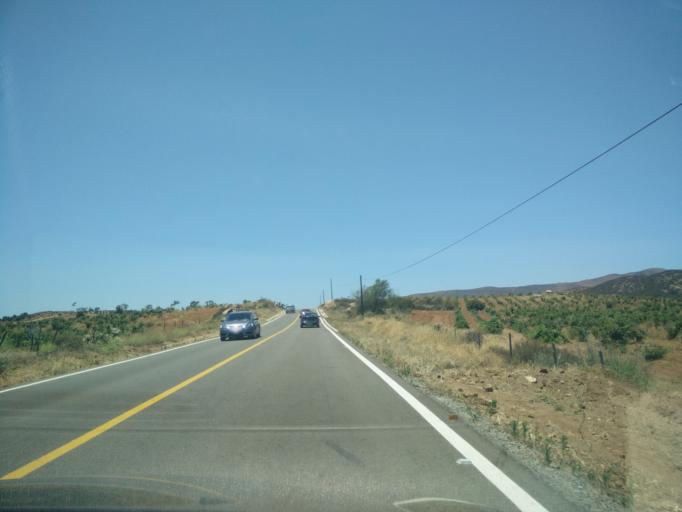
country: MX
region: Baja California
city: El Sauzal
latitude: 32.0003
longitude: -116.6642
